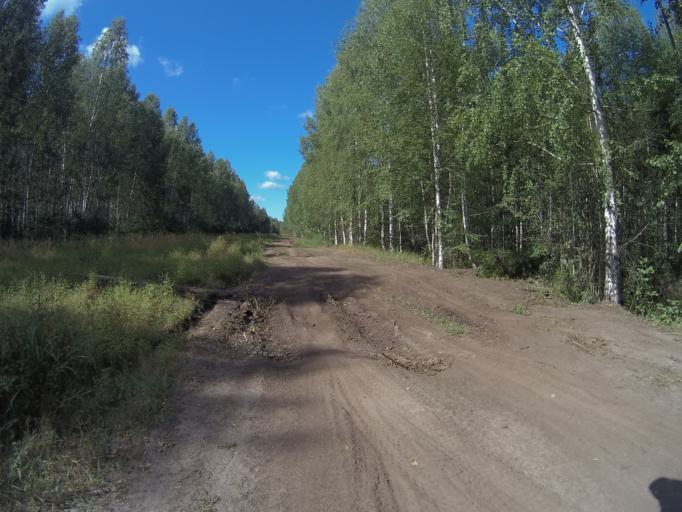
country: RU
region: Vladimir
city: Raduzhnyy
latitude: 55.9216
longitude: 40.2194
